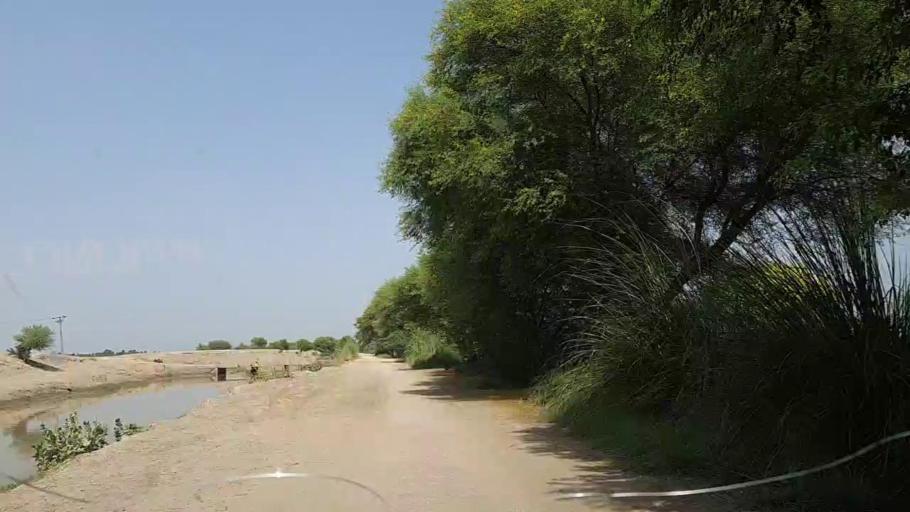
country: PK
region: Sindh
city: Ghotki
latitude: 28.0742
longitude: 69.3215
